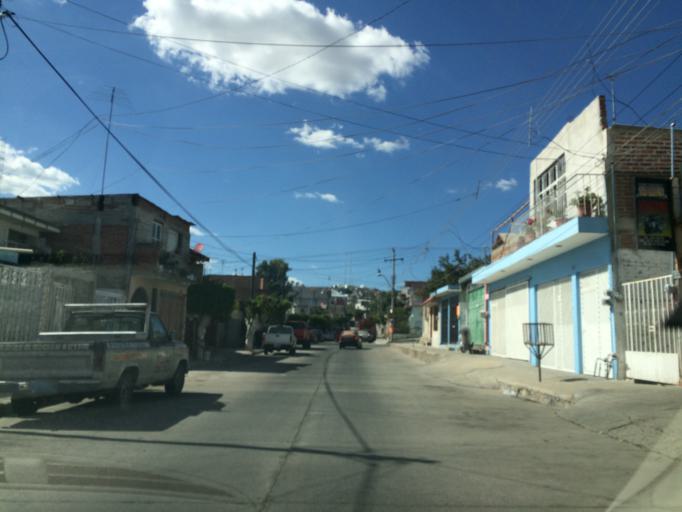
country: MX
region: Guanajuato
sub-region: Leon
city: Ejido la Joya
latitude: 21.1251
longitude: -101.7113
